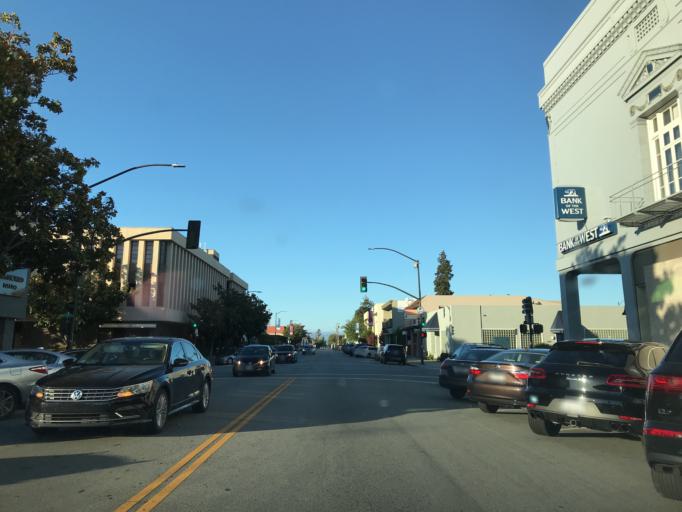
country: US
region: California
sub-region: San Mateo County
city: Burlingame
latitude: 37.5770
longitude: -122.3460
